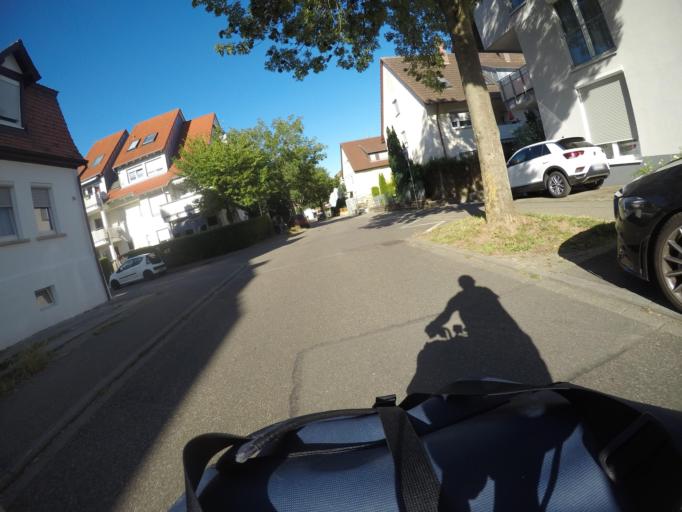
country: DE
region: Baden-Wuerttemberg
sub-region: Regierungsbezirk Stuttgart
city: Ludwigsburg
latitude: 48.8914
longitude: 9.2267
